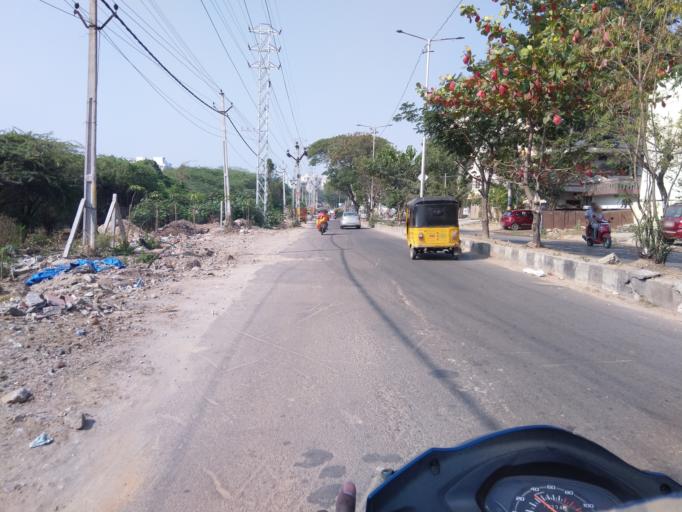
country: IN
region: Telangana
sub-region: Rangareddi
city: Kukatpalli
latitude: 17.4836
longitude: 78.3970
